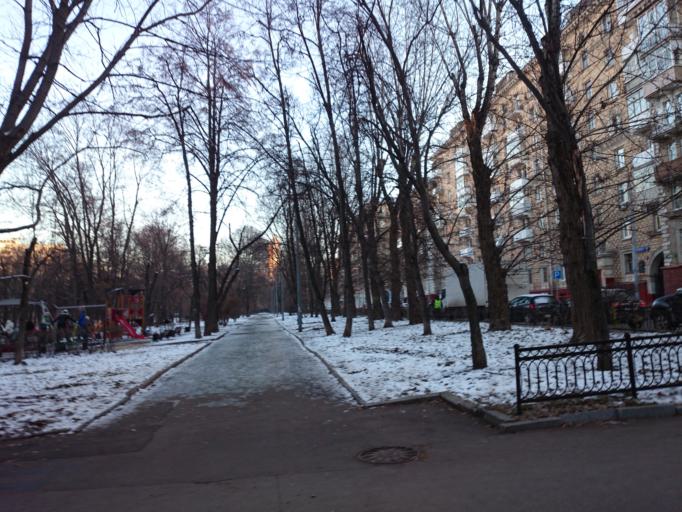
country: RU
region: Moscow
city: Sokol
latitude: 55.7958
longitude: 37.5145
